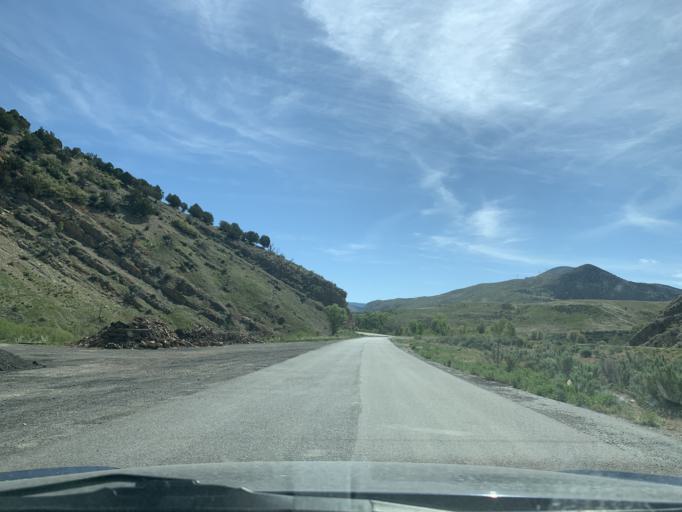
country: US
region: Utah
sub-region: Utah County
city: Woodland Hills
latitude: 39.9942
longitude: -111.4962
